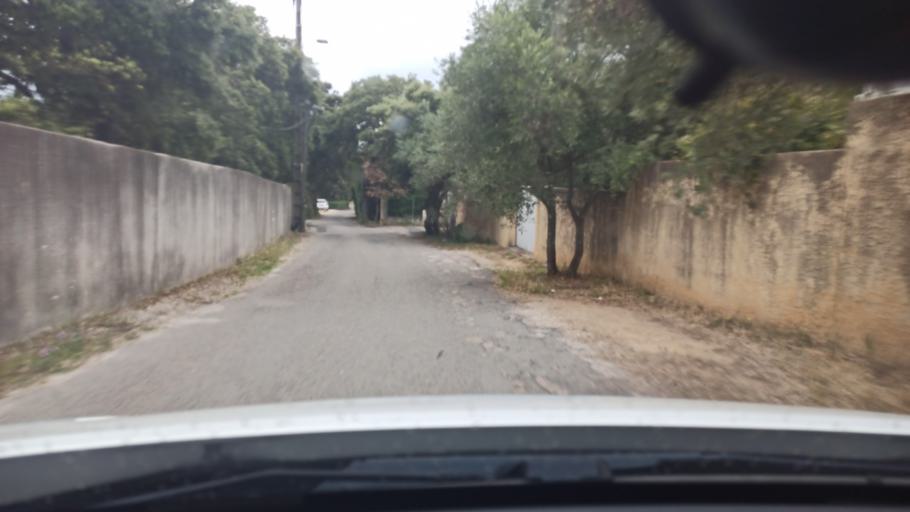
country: FR
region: Languedoc-Roussillon
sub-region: Departement du Gard
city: Les Angles
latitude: 43.9740
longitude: 4.7705
